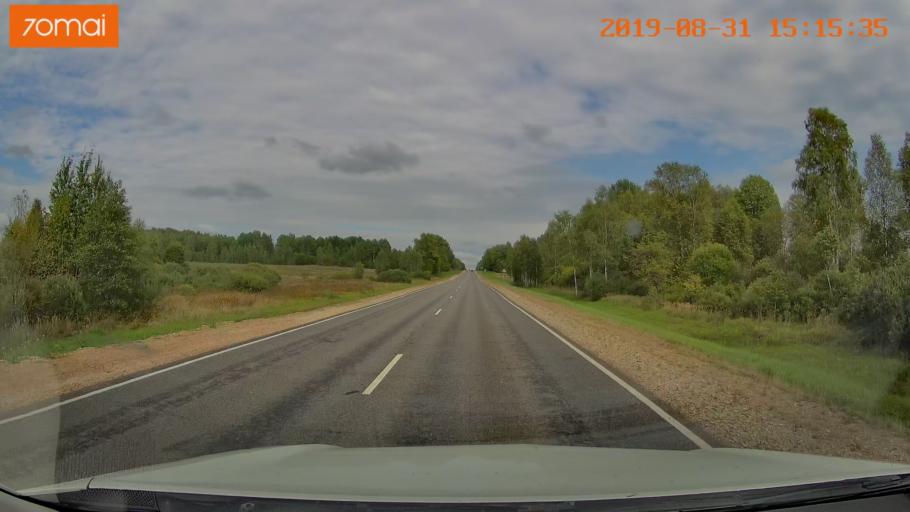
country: RU
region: Kaluga
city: Baryatino
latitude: 54.4528
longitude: 34.3299
